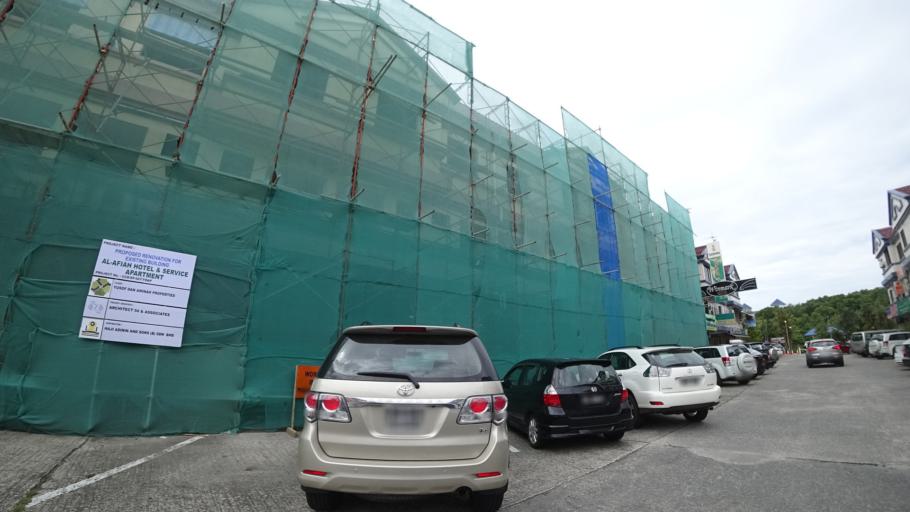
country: BN
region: Brunei and Muara
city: Bandar Seri Begawan
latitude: 4.9007
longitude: 114.9293
